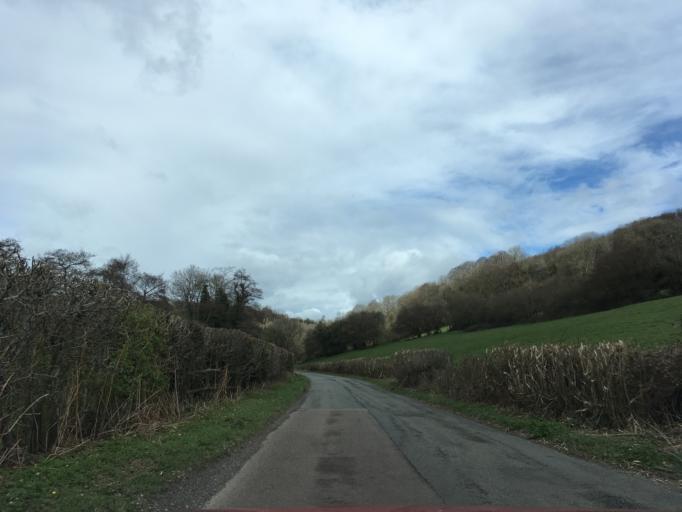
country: GB
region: England
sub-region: Gloucestershire
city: Coleford
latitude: 51.7807
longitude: -2.6322
